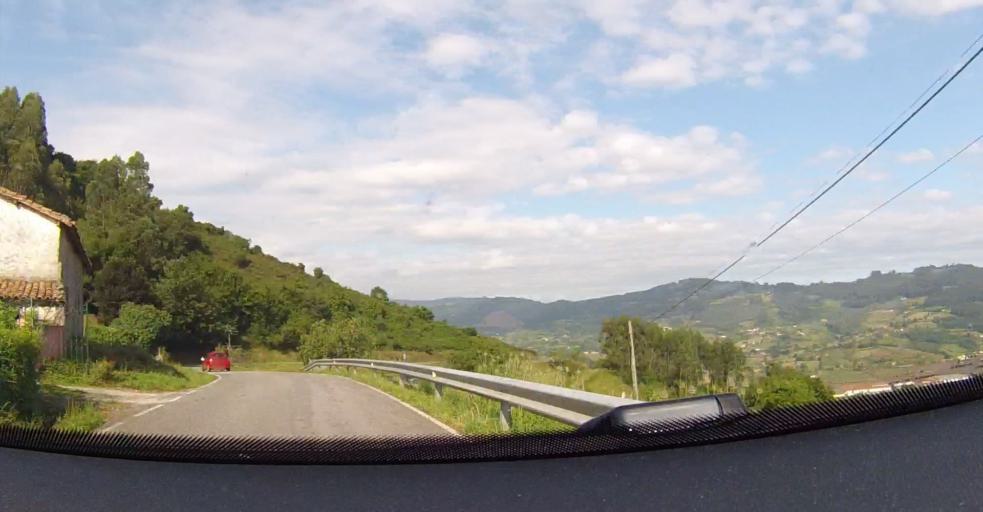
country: ES
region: Asturias
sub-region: Province of Asturias
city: Villaviciosa
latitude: 43.4861
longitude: -5.4122
